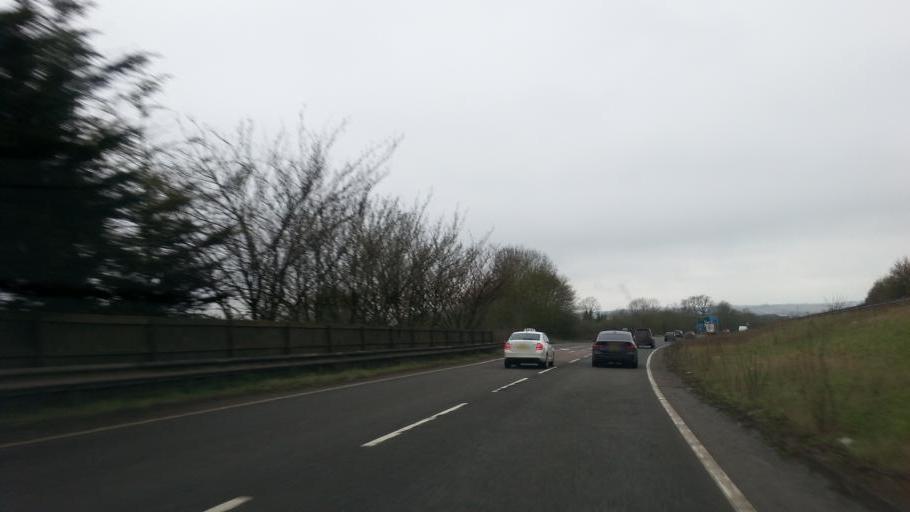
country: GB
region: England
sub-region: Oxfordshire
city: Banbury
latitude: 52.0706
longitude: -1.3023
